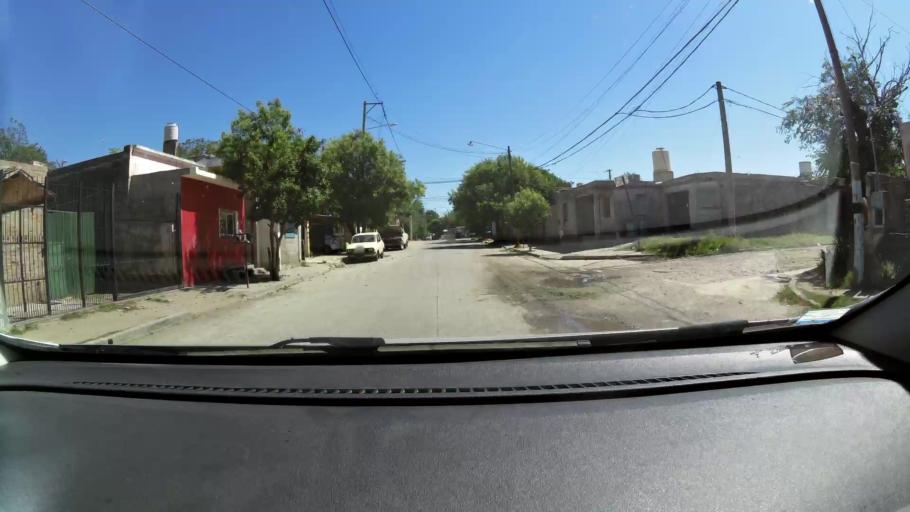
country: AR
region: Cordoba
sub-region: Departamento de Capital
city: Cordoba
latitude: -31.4131
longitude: -64.1364
